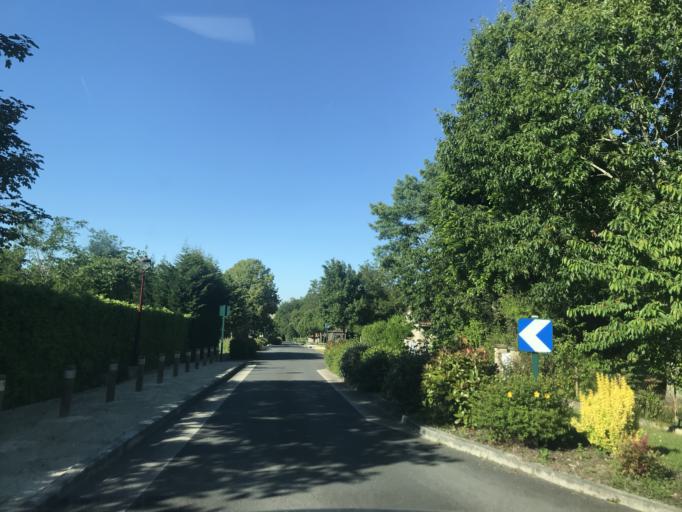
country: FR
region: Poitou-Charentes
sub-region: Departement de la Charente
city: Chalais
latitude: 45.2446
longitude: 0.0003
